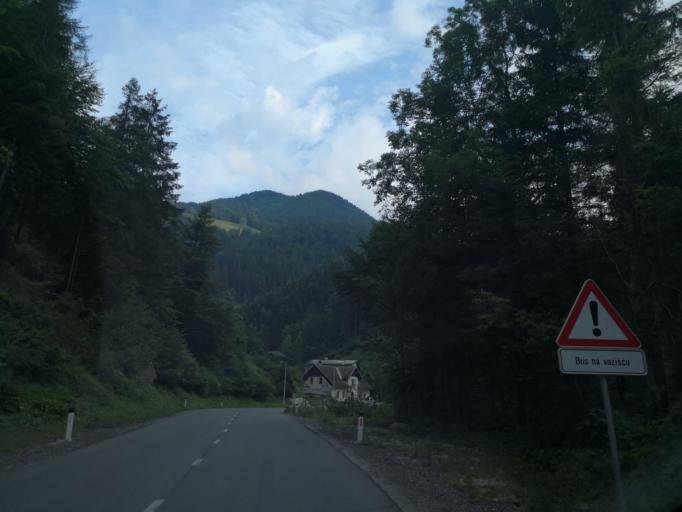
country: SI
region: Jezersko
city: Zgornje Jezersko
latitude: 46.3807
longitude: 14.4700
